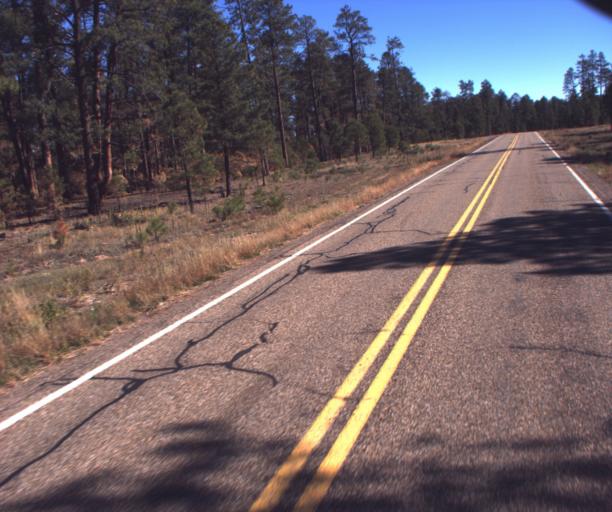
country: US
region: Arizona
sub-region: Coconino County
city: Fredonia
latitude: 36.7480
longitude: -112.2538
